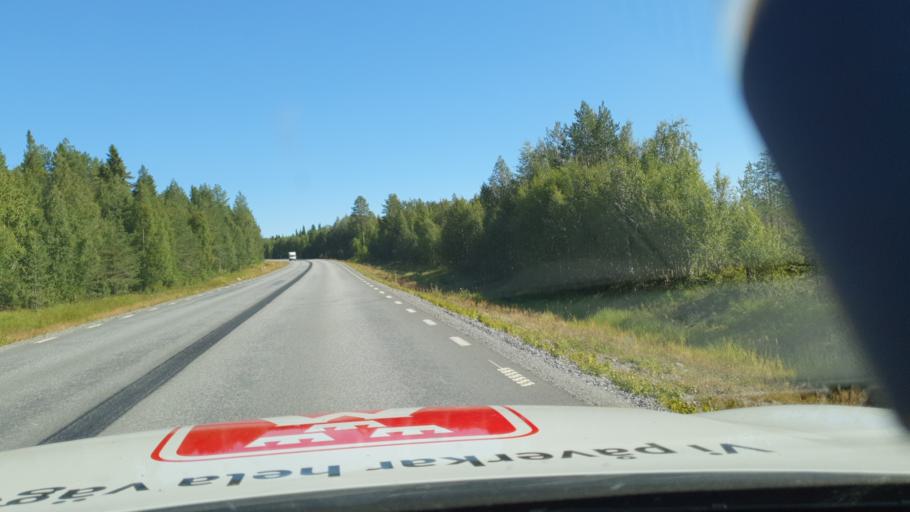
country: SE
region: Vaesterbotten
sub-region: Dorotea Kommun
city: Dorotea
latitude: 64.2887
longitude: 16.5179
